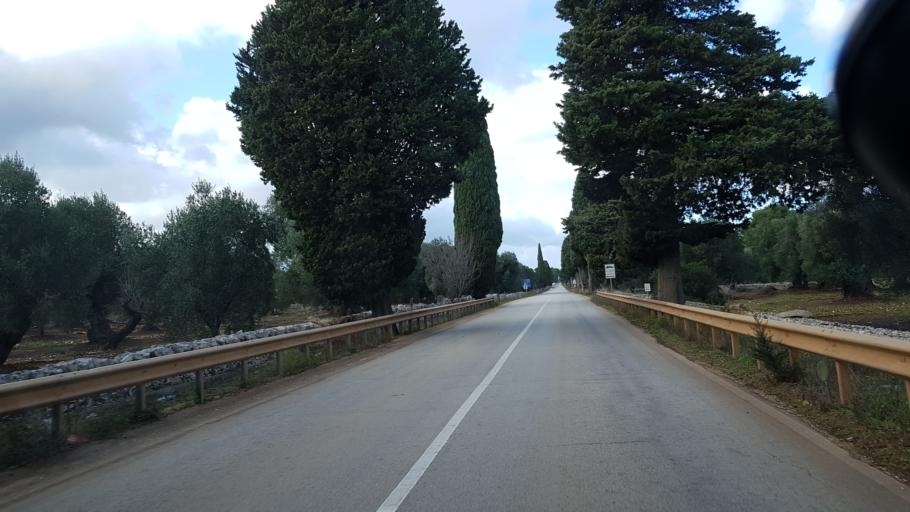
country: IT
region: Apulia
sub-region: Provincia di Brindisi
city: Montalbano
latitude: 40.7656
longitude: 17.5176
